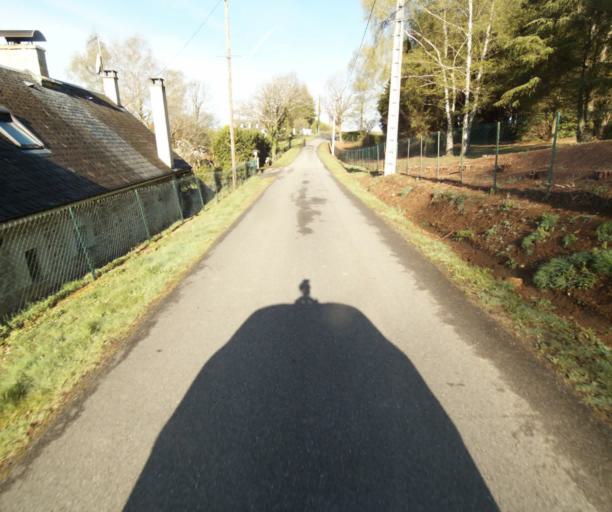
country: FR
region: Limousin
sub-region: Departement de la Correze
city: Laguenne
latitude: 45.2849
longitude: 1.8493
